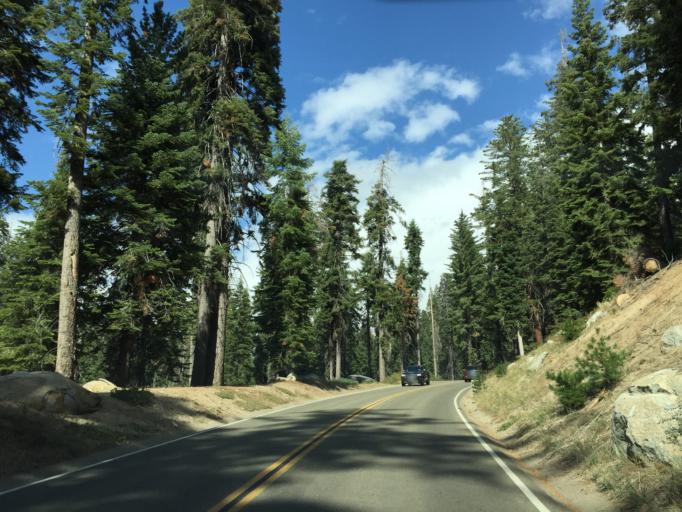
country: US
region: California
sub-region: Tulare County
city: Three Rivers
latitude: 36.5870
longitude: -118.7491
